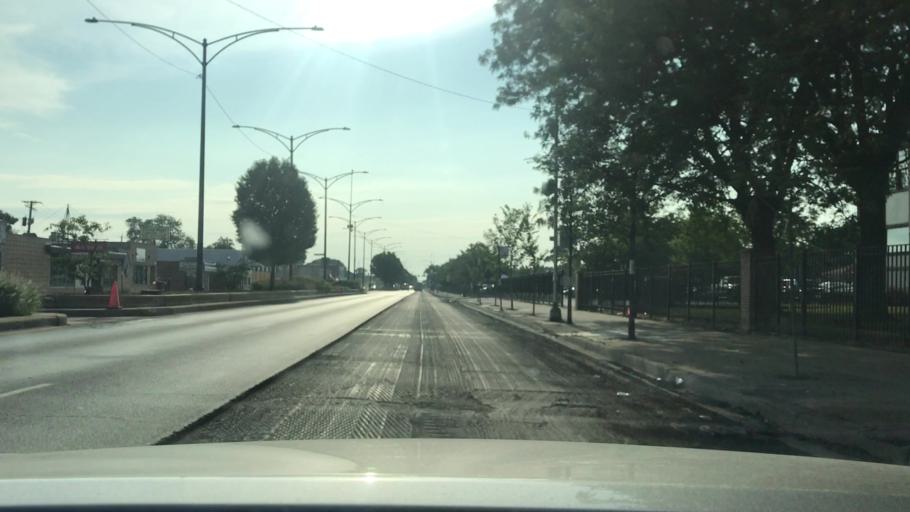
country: US
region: Illinois
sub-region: Cook County
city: Hometown
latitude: 41.7494
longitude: -87.7206
